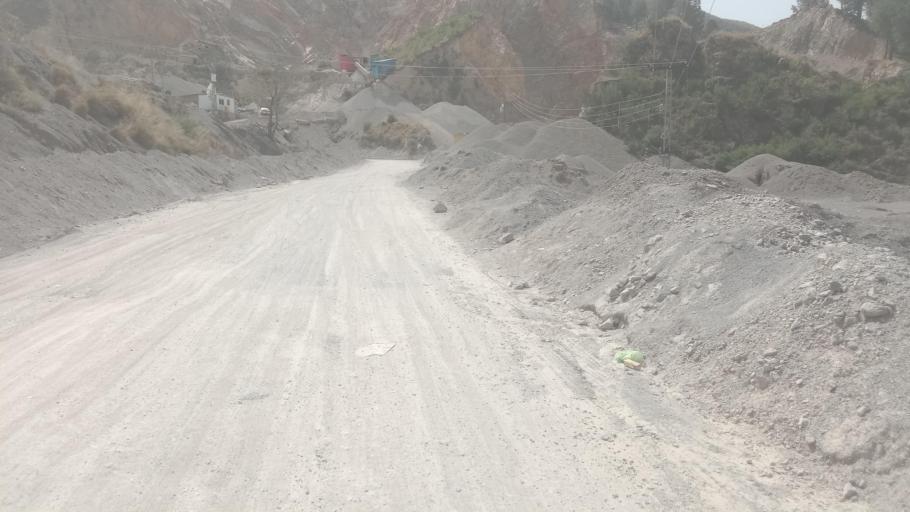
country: PK
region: Khyber Pakhtunkhwa
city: Abbottabad
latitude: 34.1621
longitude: 73.2813
